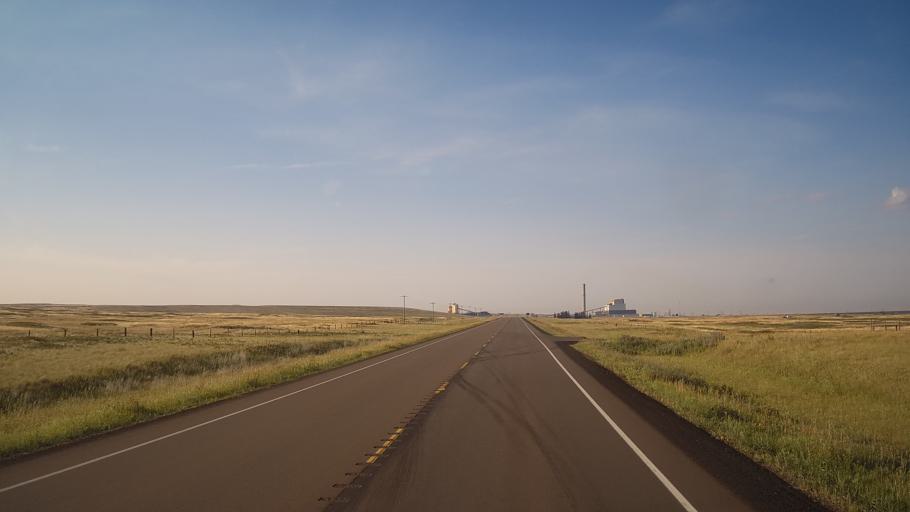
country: CA
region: Alberta
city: Hanna
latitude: 51.4700
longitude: -111.7864
